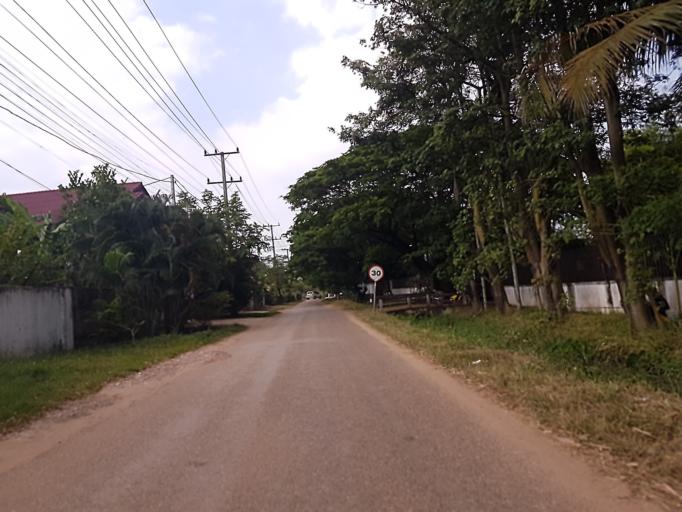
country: LA
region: Vientiane
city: Vientiane
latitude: 17.9243
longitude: 102.6273
